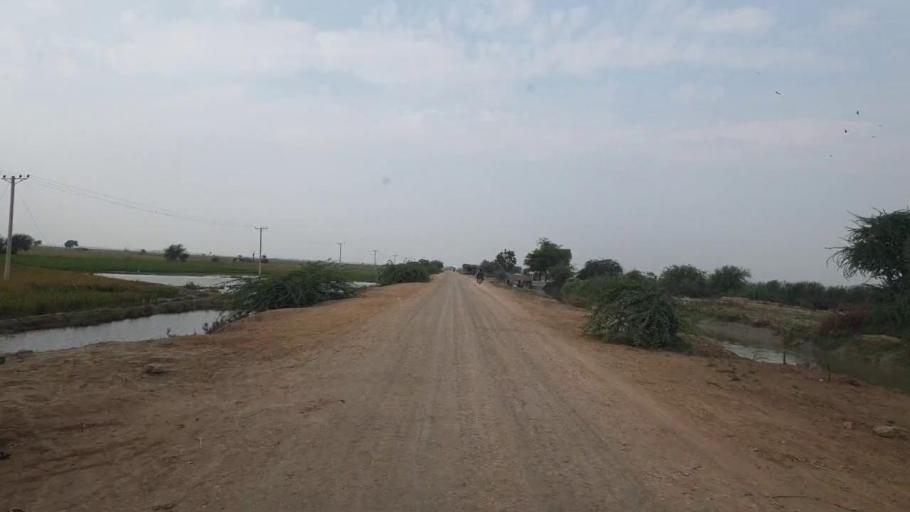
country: PK
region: Sindh
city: Kario
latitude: 24.6091
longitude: 68.5940
